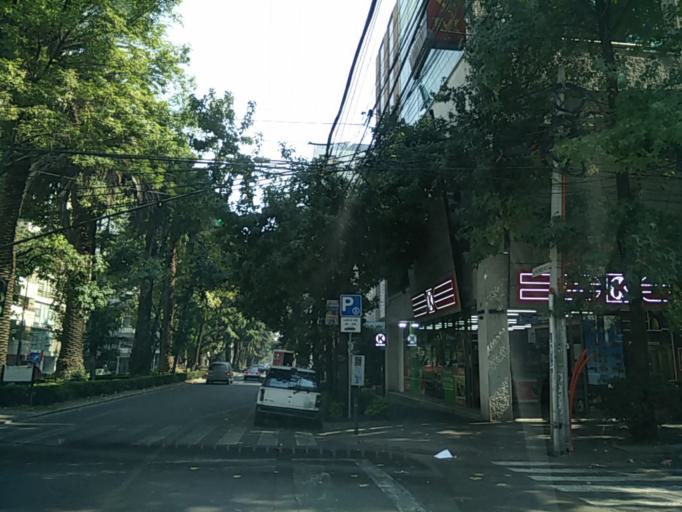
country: MX
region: Mexico City
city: Miguel Hidalgo
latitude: 19.4355
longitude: -99.1889
